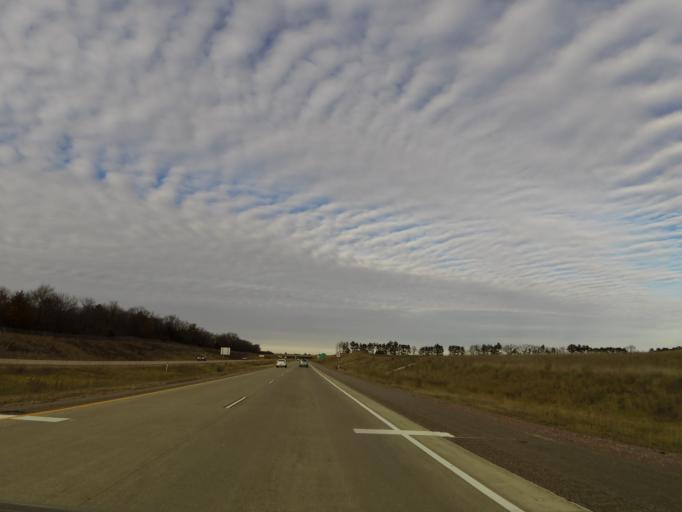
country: US
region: Wisconsin
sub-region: Sauk County
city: Lake Delton
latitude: 43.5393
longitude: -89.7870
